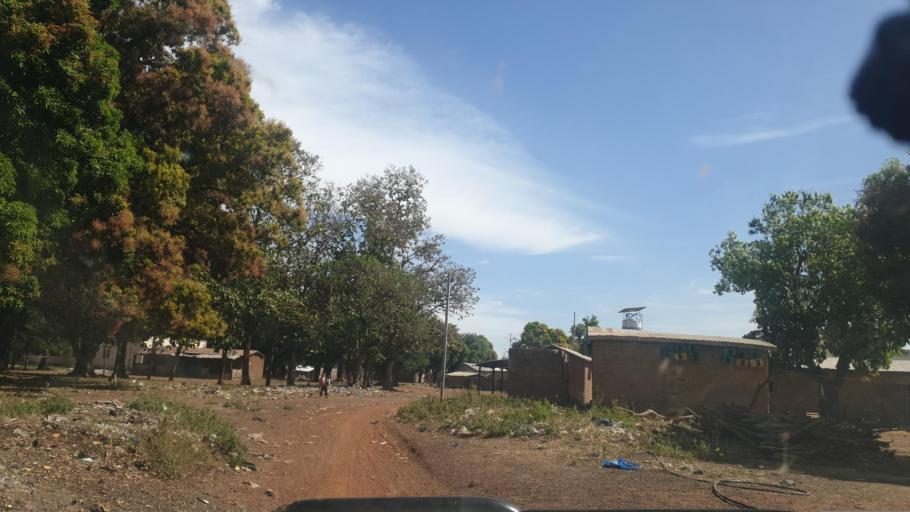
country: ML
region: Sikasso
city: Yanfolila
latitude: 10.4995
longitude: -7.9545
